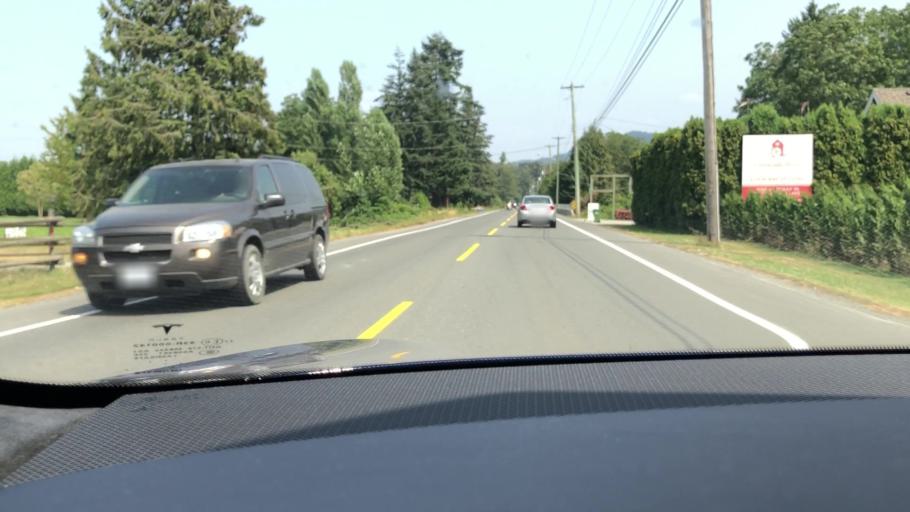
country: CA
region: British Columbia
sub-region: Fraser Valley Regional District
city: Chilliwack
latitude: 49.0893
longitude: -122.0759
